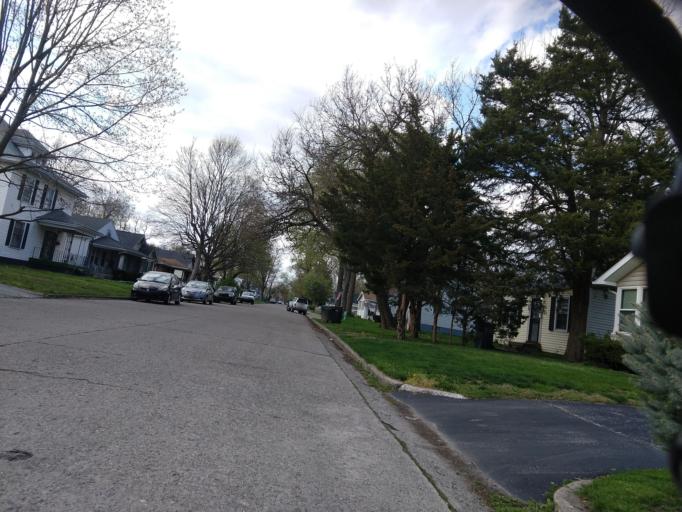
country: US
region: Indiana
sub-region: Marion County
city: Broad Ripple
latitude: 39.8368
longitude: -86.1277
